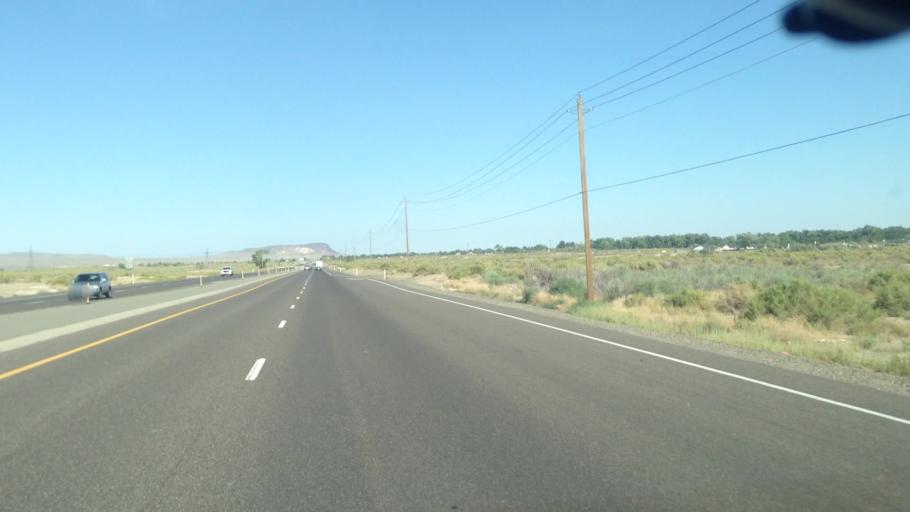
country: US
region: Nevada
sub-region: Lyon County
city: Fernley
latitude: 39.5969
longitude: -119.1871
